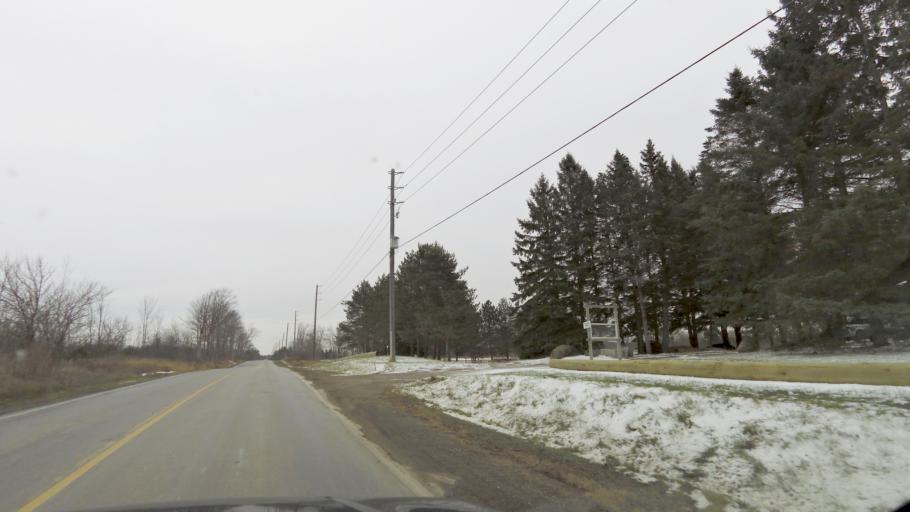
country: CA
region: Ontario
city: Vaughan
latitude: 43.8718
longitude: -79.6147
